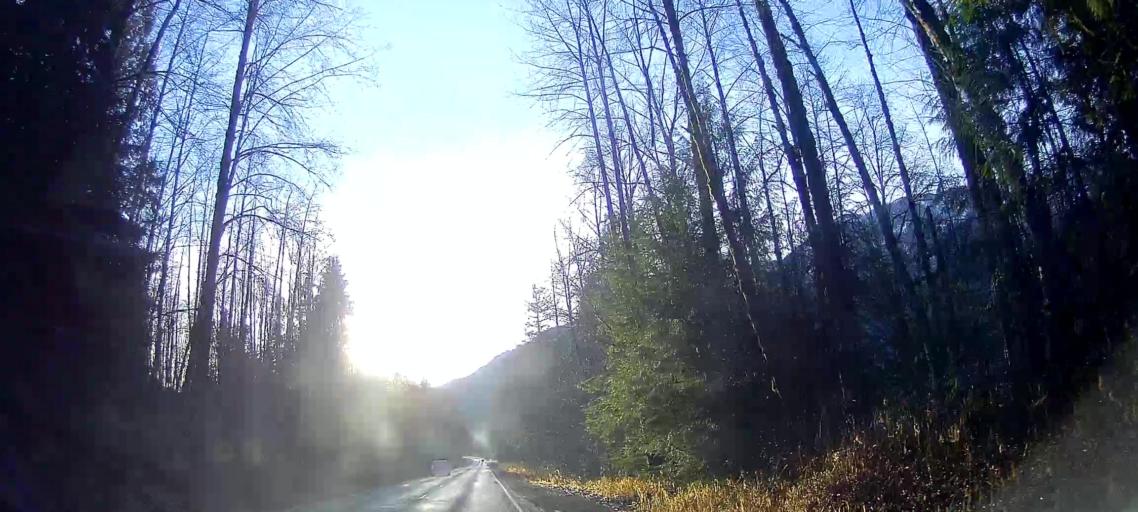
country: US
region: Washington
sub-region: Snohomish County
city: Darrington
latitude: 48.6045
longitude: -121.7601
